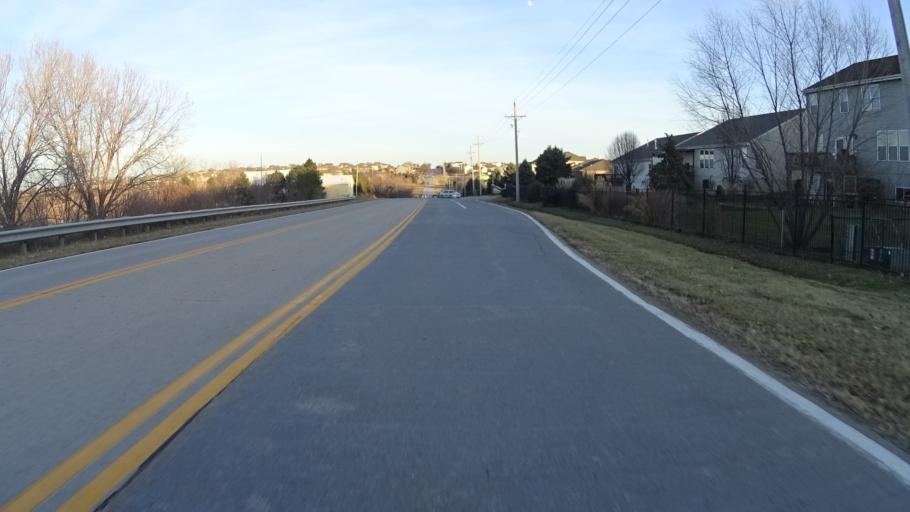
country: US
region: Nebraska
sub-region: Sarpy County
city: Papillion
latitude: 41.1326
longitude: -96.0700
